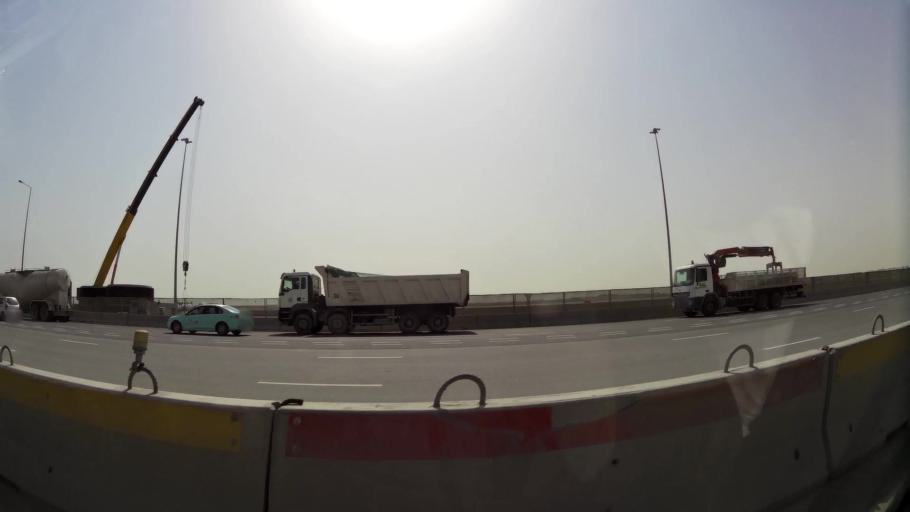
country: QA
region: Baladiyat ad Dawhah
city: Doha
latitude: 25.2195
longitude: 51.5034
